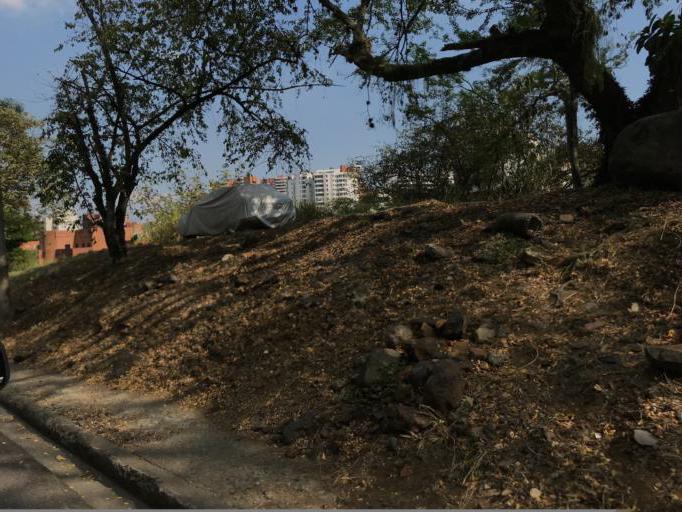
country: CO
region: Valle del Cauca
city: Cali
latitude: 3.4508
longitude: -76.5563
